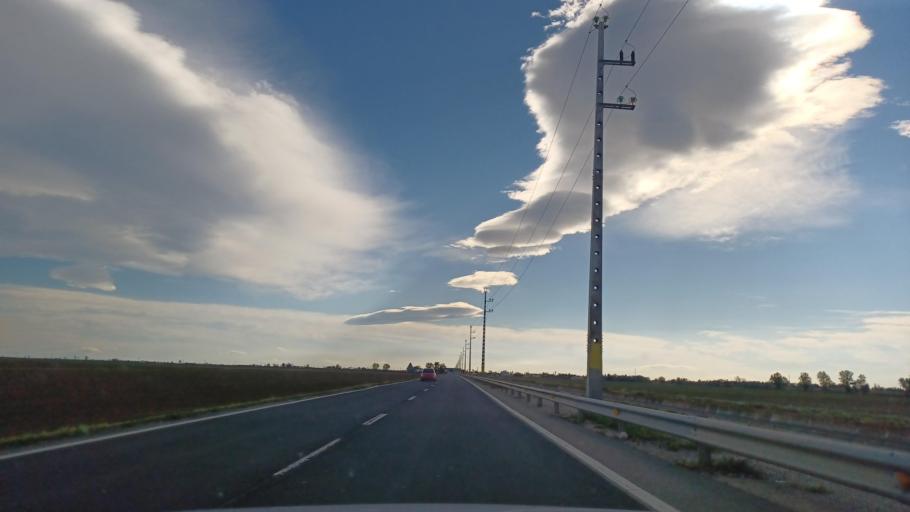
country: ES
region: Catalonia
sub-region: Provincia de Tarragona
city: Deltebre
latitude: 40.7230
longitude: 0.6593
